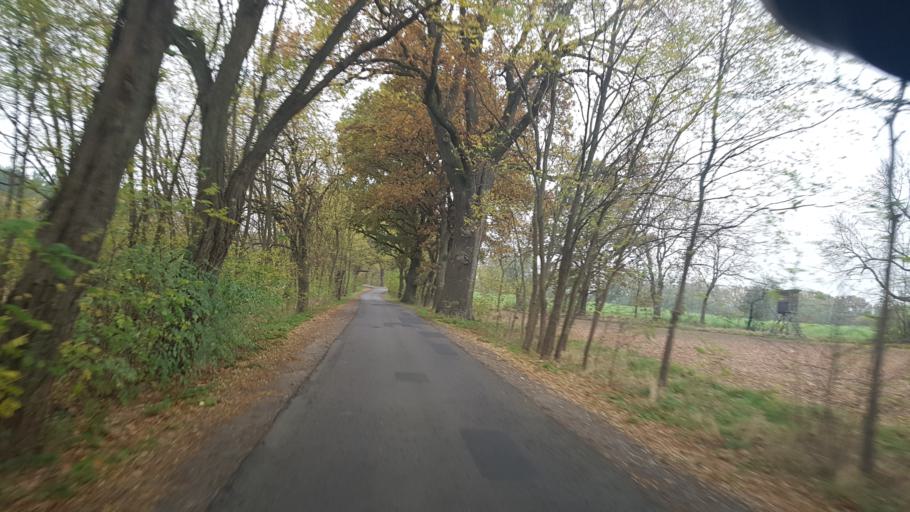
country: DE
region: Brandenburg
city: Lindow
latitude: 52.9453
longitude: 13.0524
